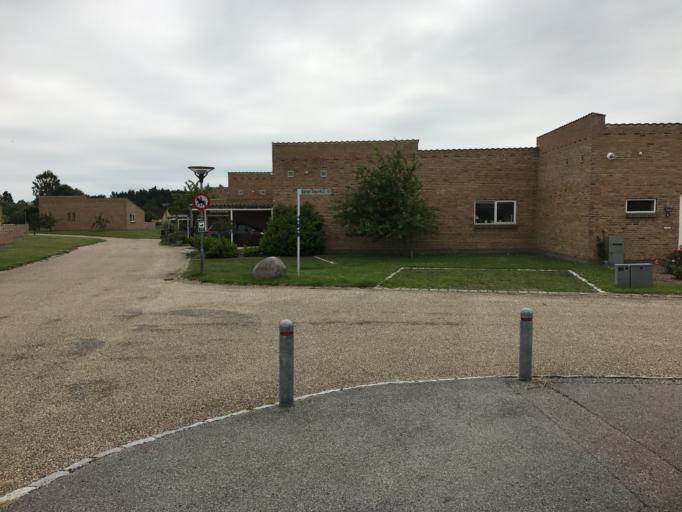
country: DK
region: Capital Region
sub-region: Allerod Kommune
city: Lynge
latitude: 55.8391
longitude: 12.2800
